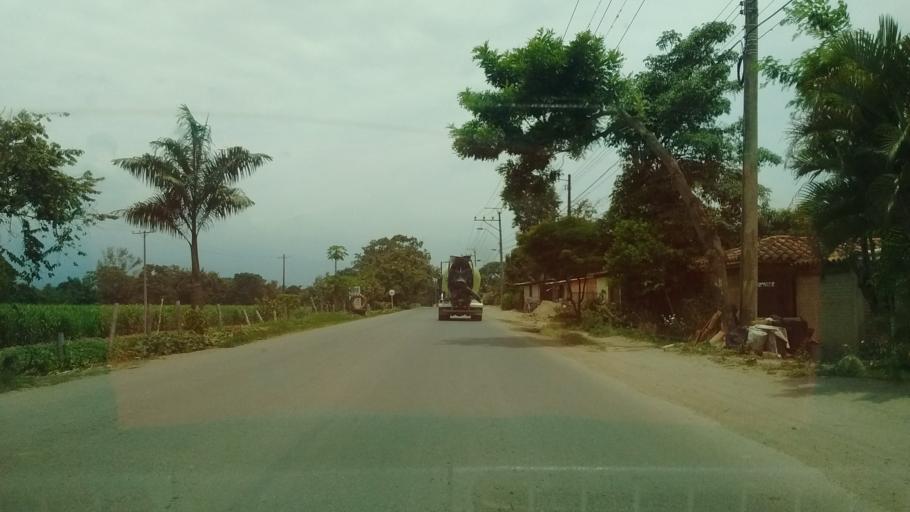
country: CO
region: Valle del Cauca
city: Jamundi
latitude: 3.3146
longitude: -76.4891
